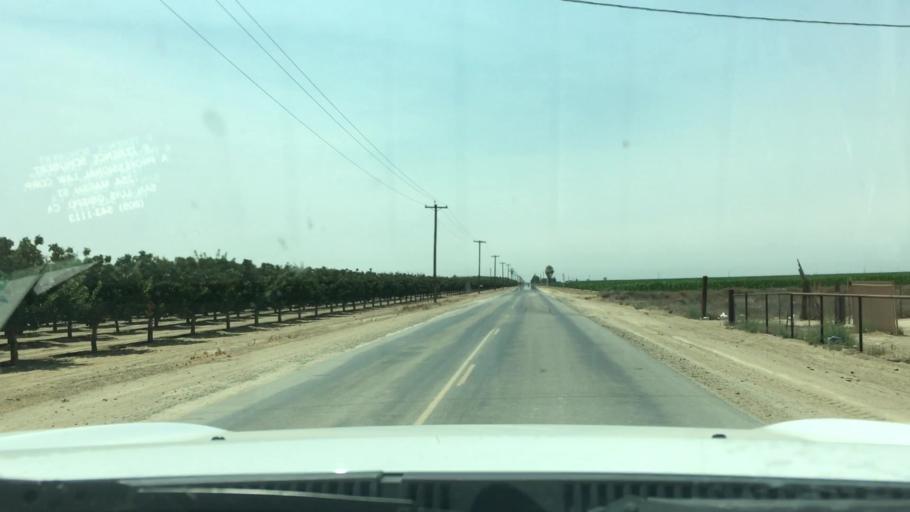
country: US
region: California
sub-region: Kern County
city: Wasco
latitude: 35.6788
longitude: -119.4374
